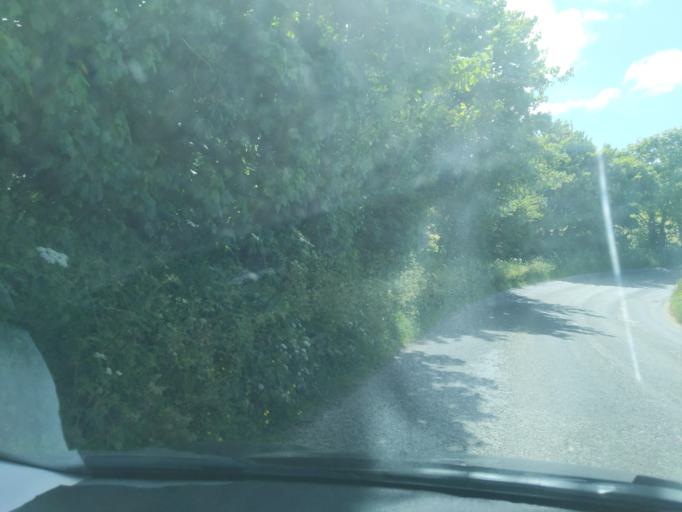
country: GB
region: England
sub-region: Cornwall
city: Perranporth
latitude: 50.2973
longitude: -5.1387
